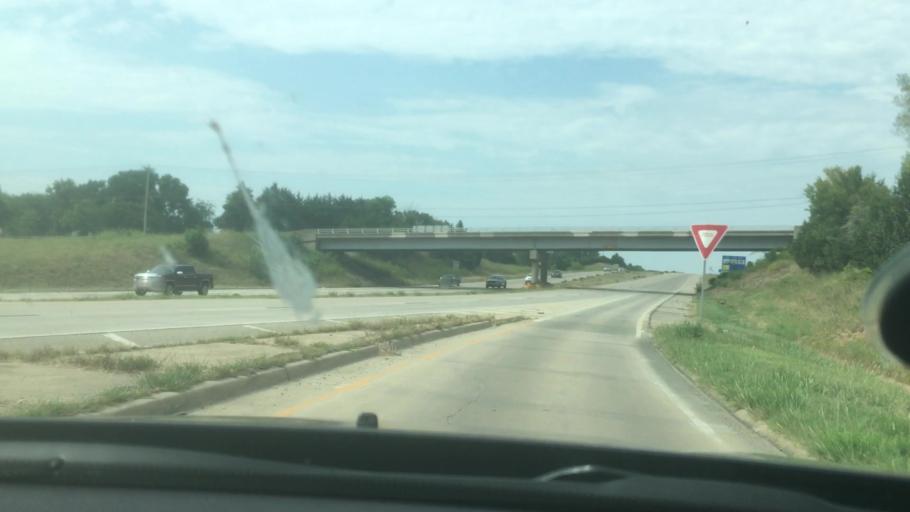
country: US
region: Oklahoma
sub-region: Pontotoc County
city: Ada
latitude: 34.7786
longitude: -96.7005
